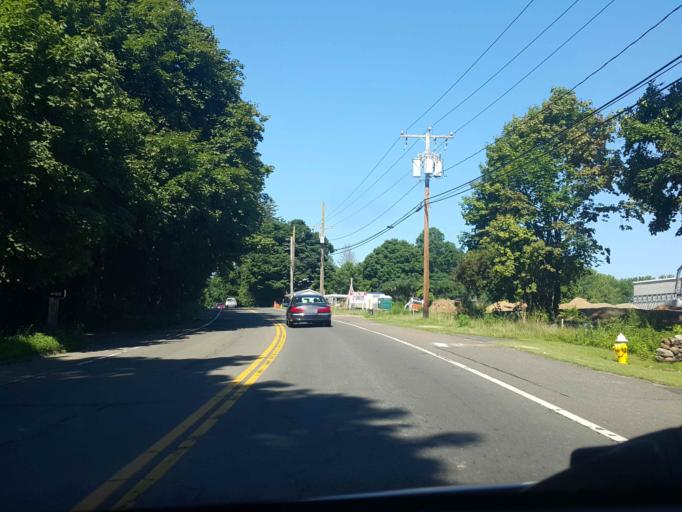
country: US
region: Connecticut
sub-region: New Haven County
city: North Branford
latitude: 41.3119
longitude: -72.7408
